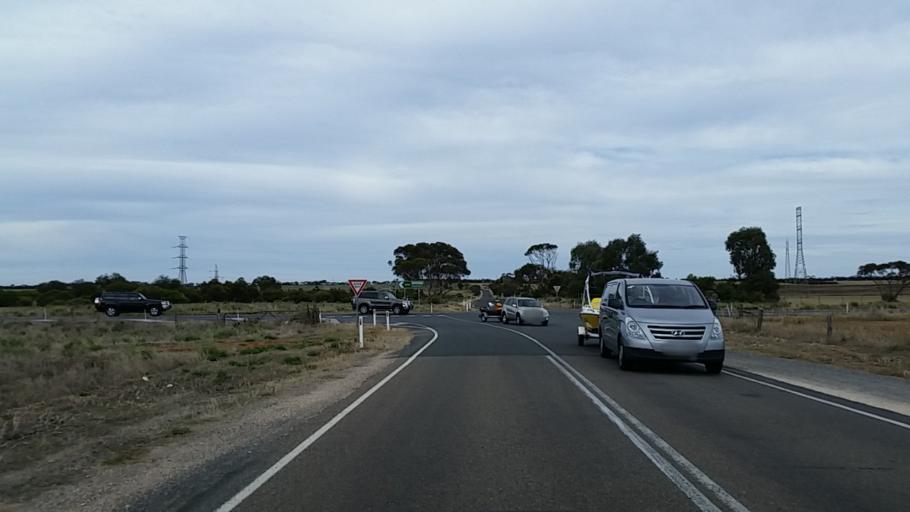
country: AU
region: South Australia
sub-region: Murray Bridge
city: Murray Bridge
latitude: -35.0141
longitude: 139.2512
